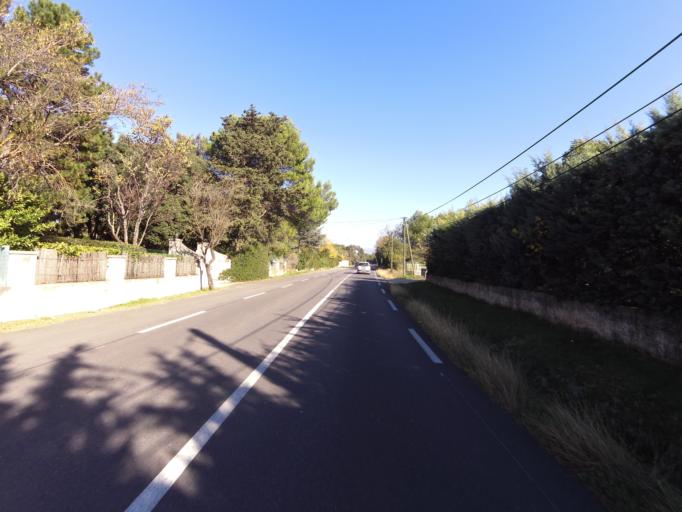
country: FR
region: Provence-Alpes-Cote d'Azur
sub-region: Departement du Vaucluse
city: Carpentras
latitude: 44.0687
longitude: 5.0726
